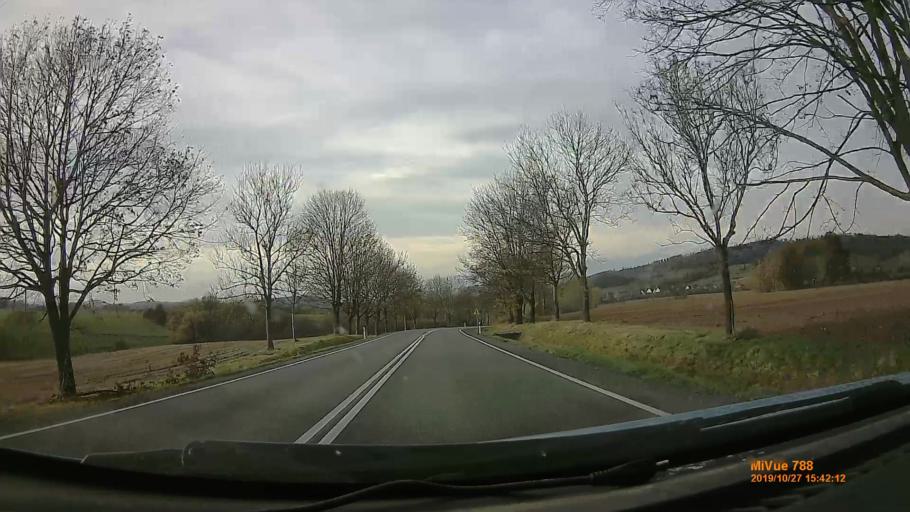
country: PL
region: Lower Silesian Voivodeship
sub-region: Powiat klodzki
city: Klodzko
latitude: 50.4564
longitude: 16.6302
